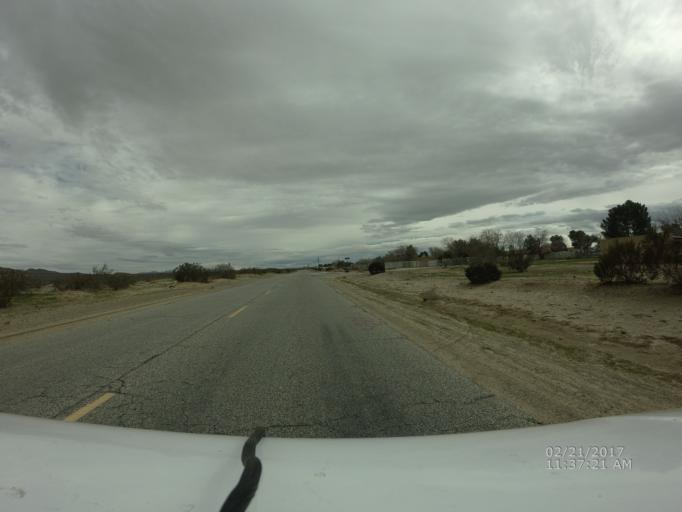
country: US
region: California
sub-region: Los Angeles County
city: Lake Los Angeles
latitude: 34.6312
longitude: -117.8322
